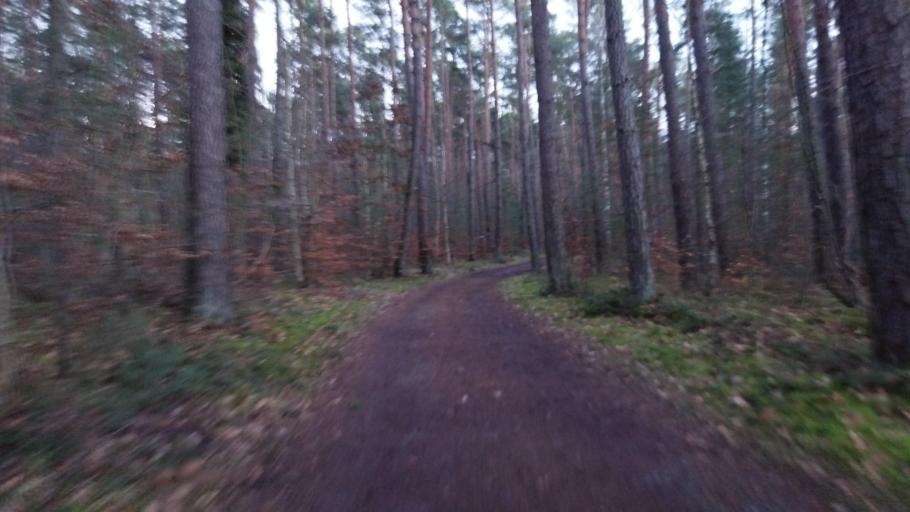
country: DE
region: Rheinland-Pfalz
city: Dudenhofen
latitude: 49.3257
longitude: 8.3698
